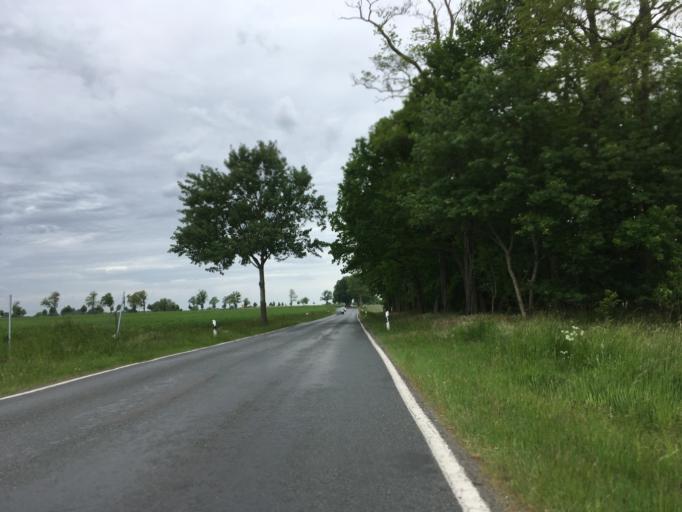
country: DE
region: Brandenburg
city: Bernau bei Berlin
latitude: 52.6686
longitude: 13.6382
